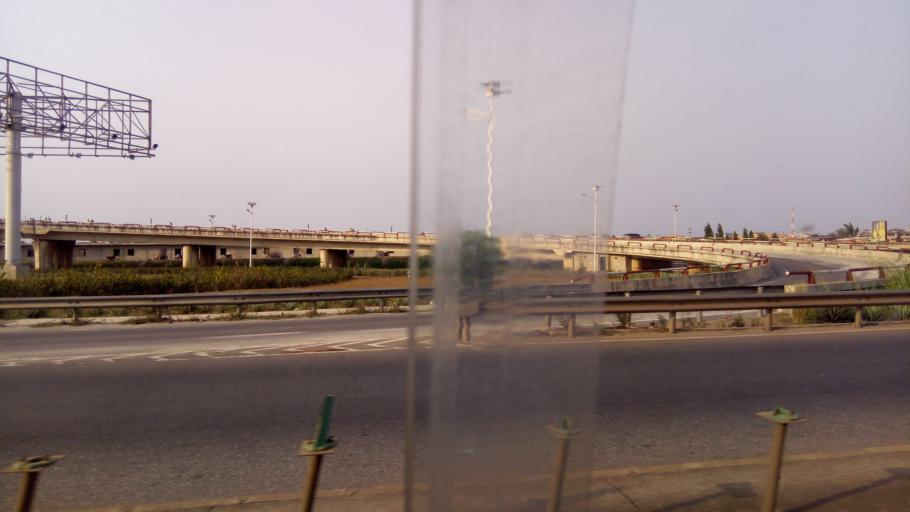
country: BJ
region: Atlantique
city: Abomey-Calavi
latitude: 6.3895
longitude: 2.3544
